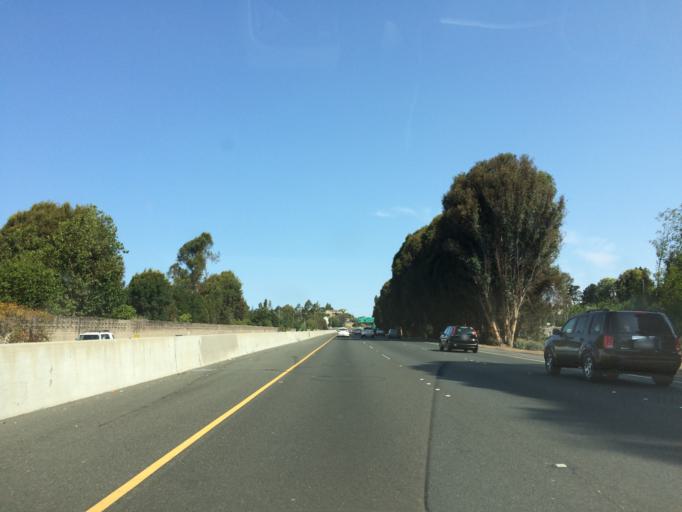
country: US
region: California
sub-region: Solano County
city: Vallejo
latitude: 38.1169
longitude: -122.2301
